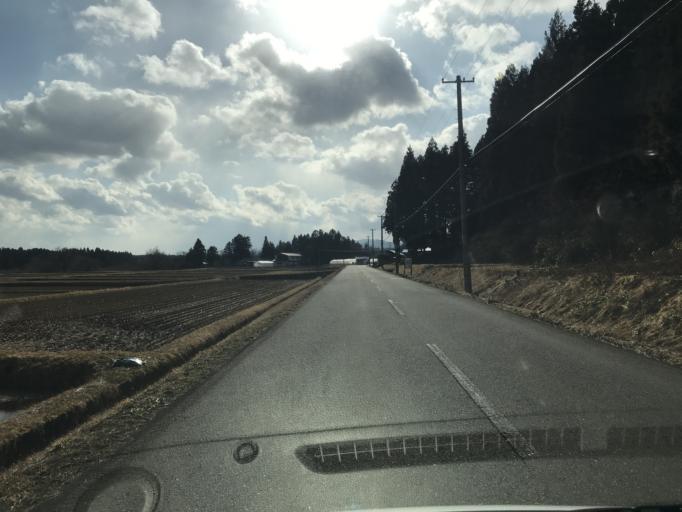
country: JP
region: Iwate
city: Mizusawa
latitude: 39.1475
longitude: 141.0406
